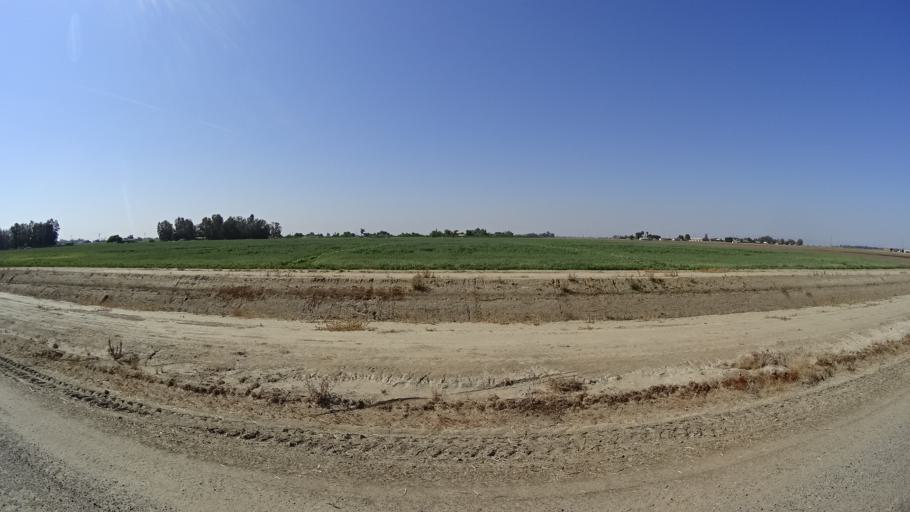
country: US
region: California
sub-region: Fresno County
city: Riverdale
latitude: 36.3512
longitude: -119.8730
